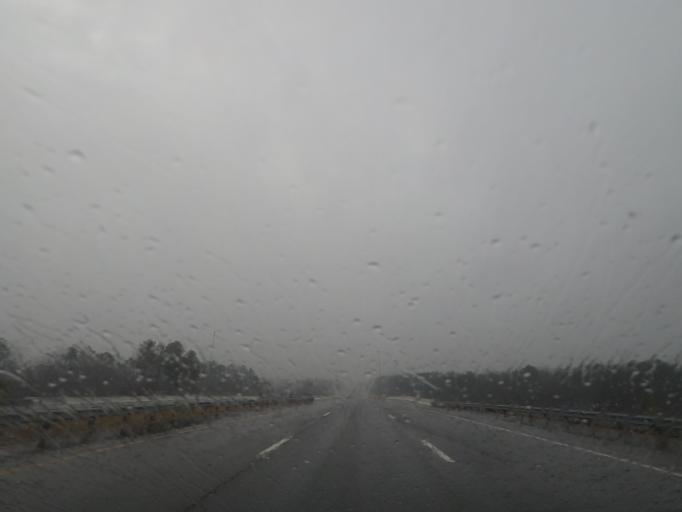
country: US
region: North Carolina
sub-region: Wake County
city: Morrisville
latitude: 35.8714
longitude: -78.8659
